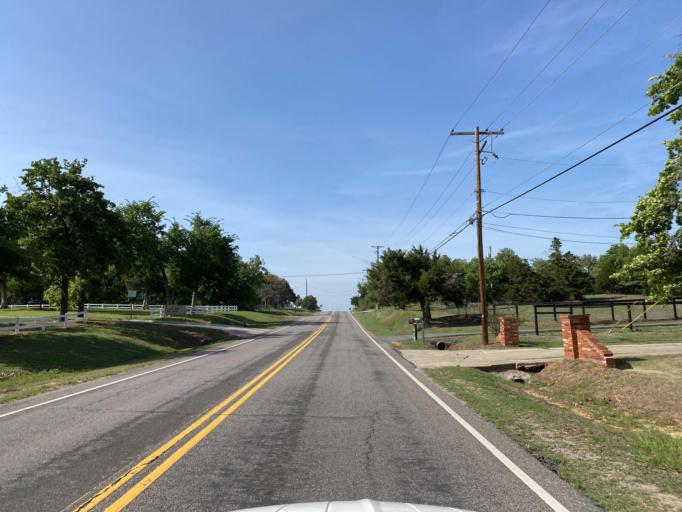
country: US
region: Oklahoma
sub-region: Oklahoma County
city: Nicoma Park
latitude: 35.4546
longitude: -97.3357
